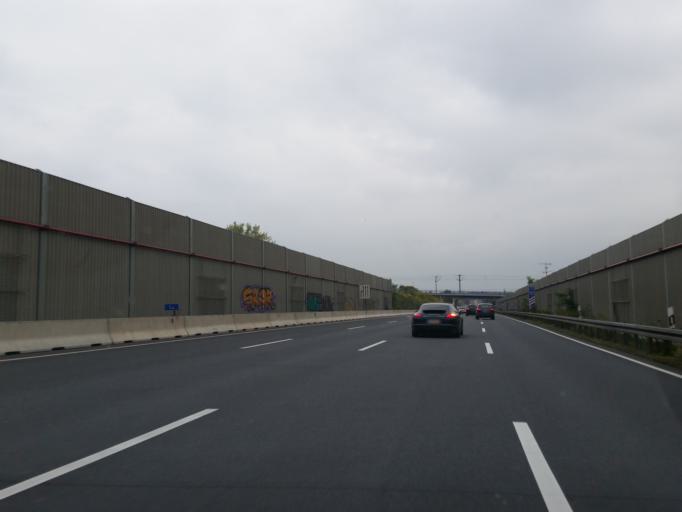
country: DE
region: Lower Saxony
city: Braunschweig
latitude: 52.2376
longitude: 10.5094
